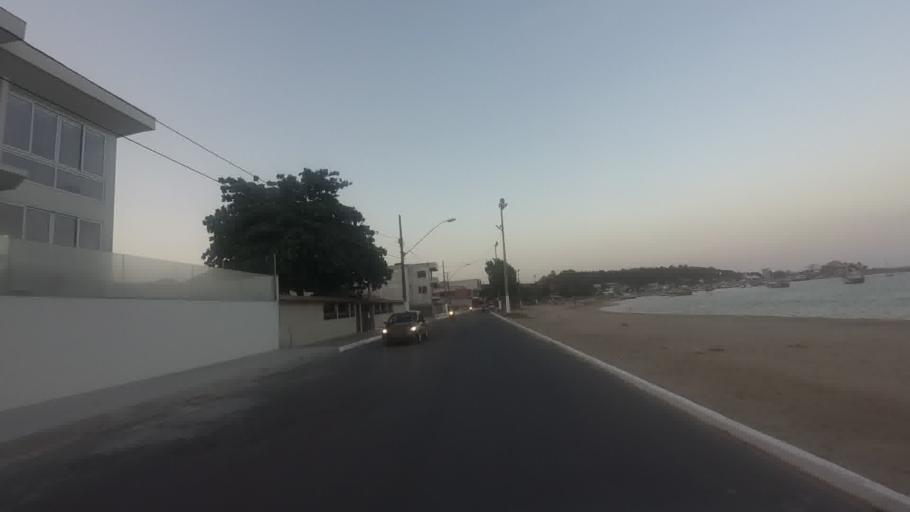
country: BR
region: Espirito Santo
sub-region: Piuma
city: Piuma
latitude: -20.8935
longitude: -40.7740
